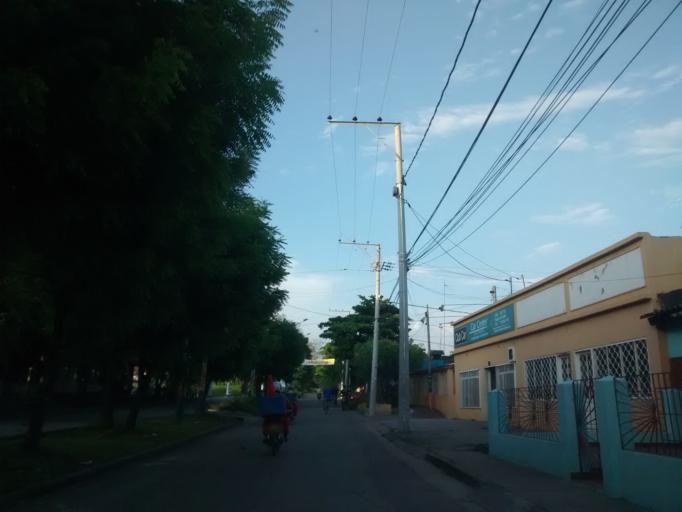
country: CO
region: Cundinamarca
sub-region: Girardot
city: Girardot City
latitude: 4.3162
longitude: -74.7919
